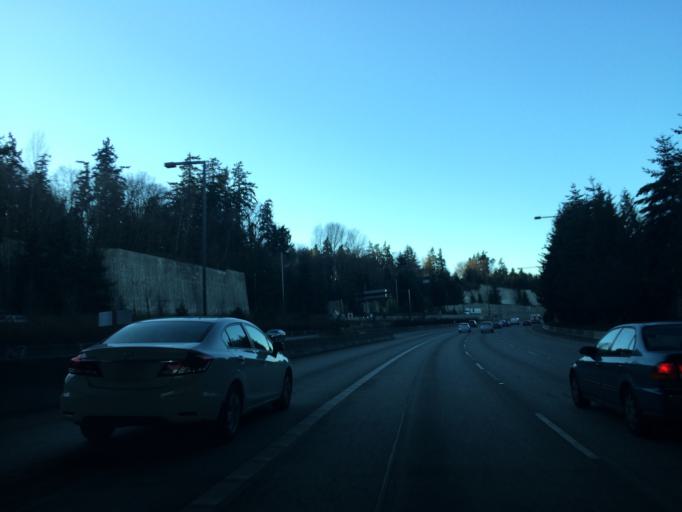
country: US
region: Washington
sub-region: King County
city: Mercer Island
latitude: 47.5791
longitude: -122.2127
